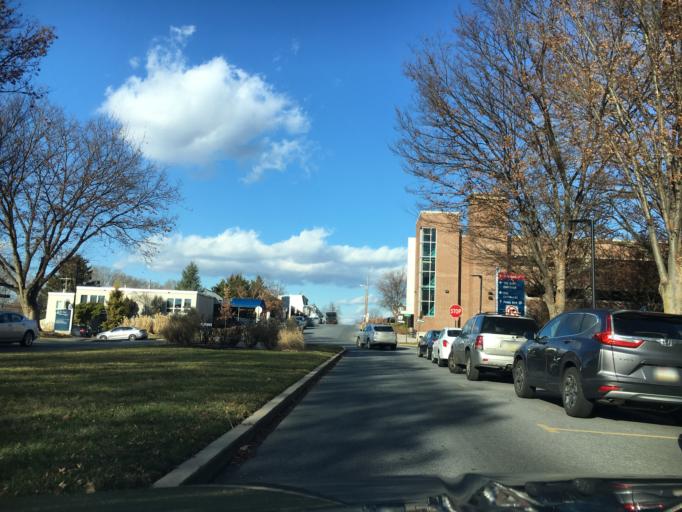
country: US
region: Pennsylvania
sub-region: Berks County
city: West Reading
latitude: 40.3320
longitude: -75.9500
